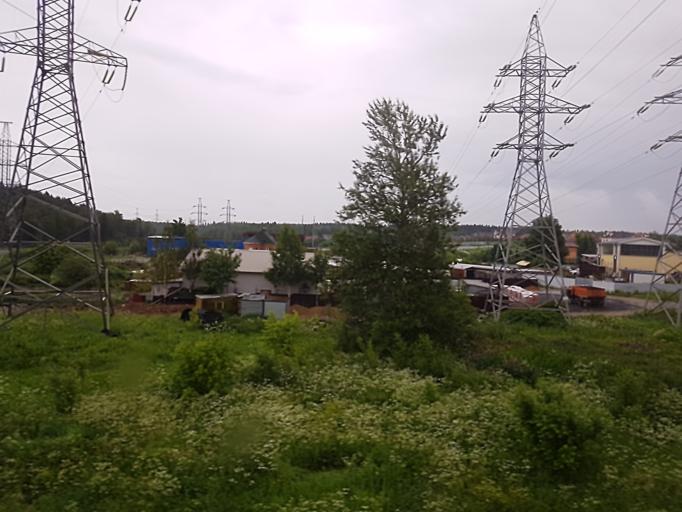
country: RU
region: Moskovskaya
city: Lesnoy Gorodok
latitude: 55.6381
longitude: 37.2306
